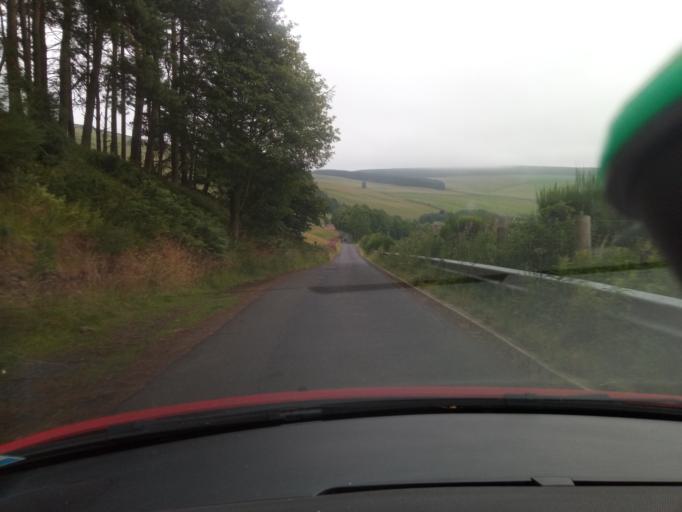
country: GB
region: Scotland
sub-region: The Scottish Borders
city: Galashiels
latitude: 55.6987
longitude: -2.8838
